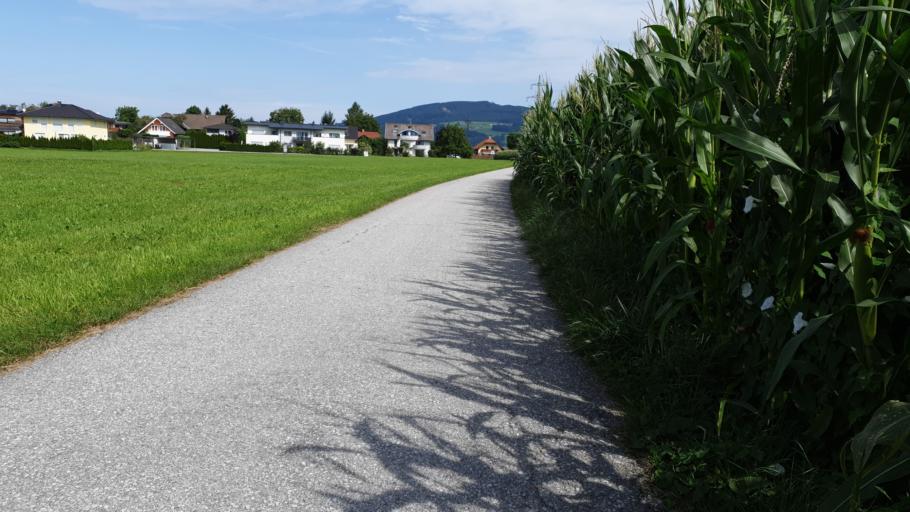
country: AT
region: Salzburg
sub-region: Politischer Bezirk Salzburg-Umgebung
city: Anthering
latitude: 47.8581
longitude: 13.0132
